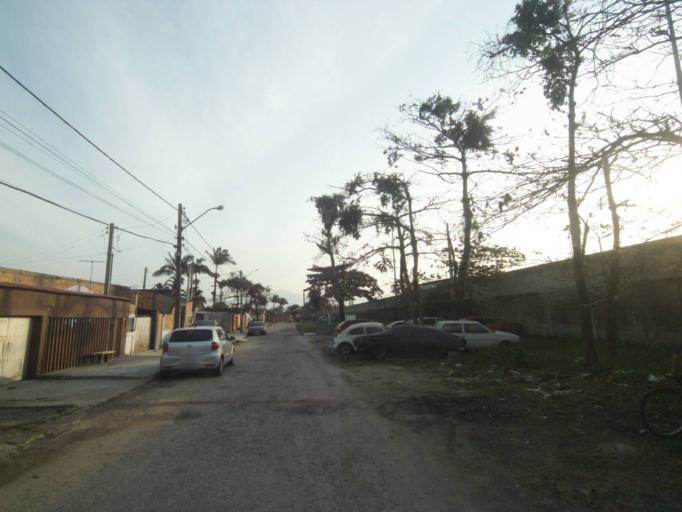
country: BR
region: Parana
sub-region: Paranagua
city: Paranagua
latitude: -25.5121
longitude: -48.5387
